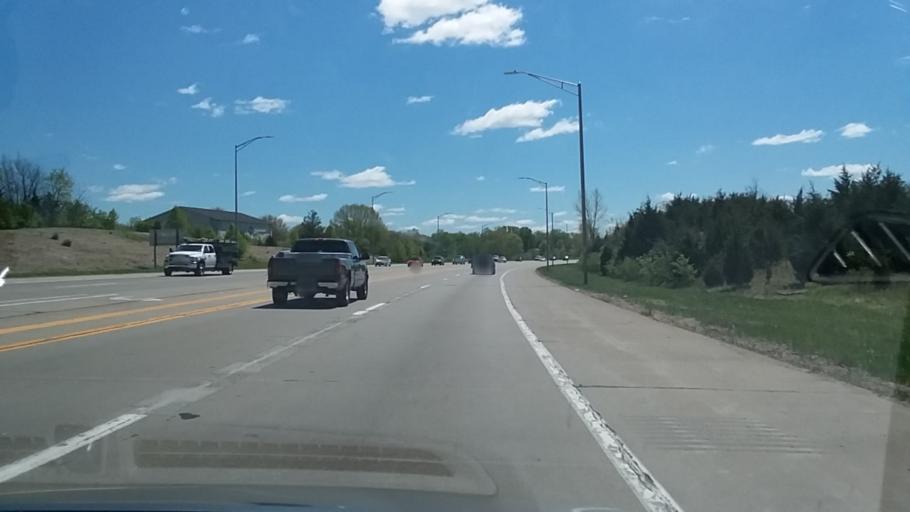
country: US
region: Kansas
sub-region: Johnson County
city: Olathe
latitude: 38.8957
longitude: -94.8372
